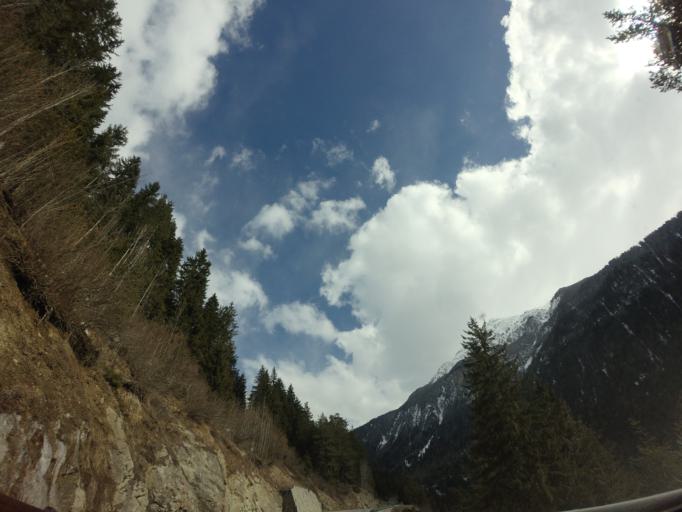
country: CH
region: Grisons
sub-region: Inn District
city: Scuol
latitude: 46.8357
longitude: 10.4052
